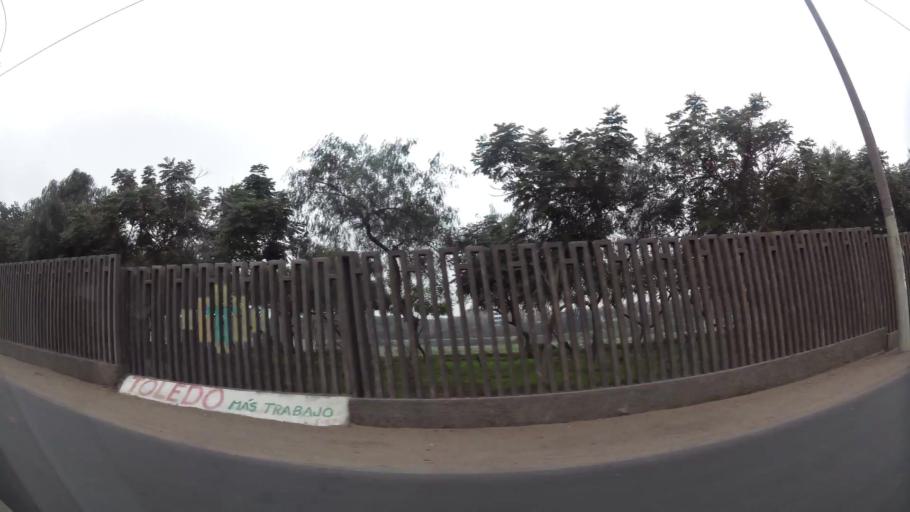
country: PE
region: Lima
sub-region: Lima
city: Vitarte
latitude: -12.0239
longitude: -76.9623
